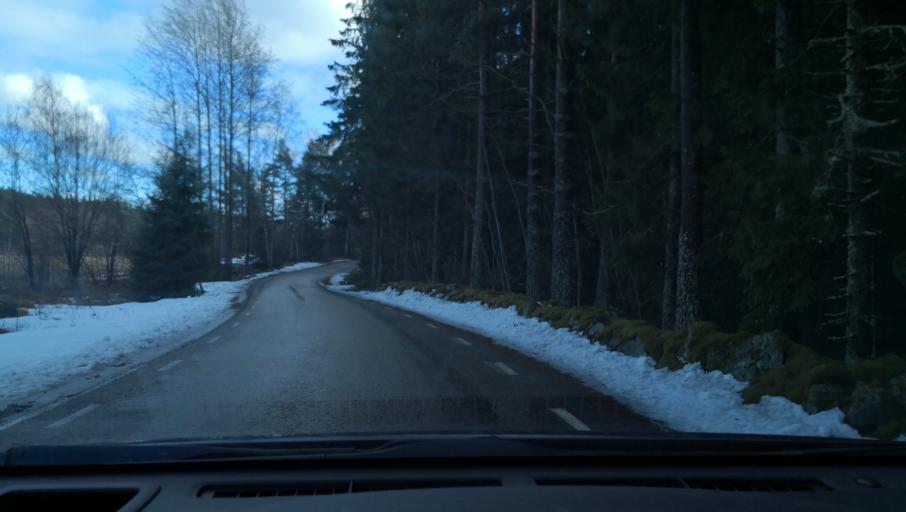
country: SE
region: Vaestmanland
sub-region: Arboga Kommun
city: Arboga
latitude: 59.3186
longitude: 15.7606
